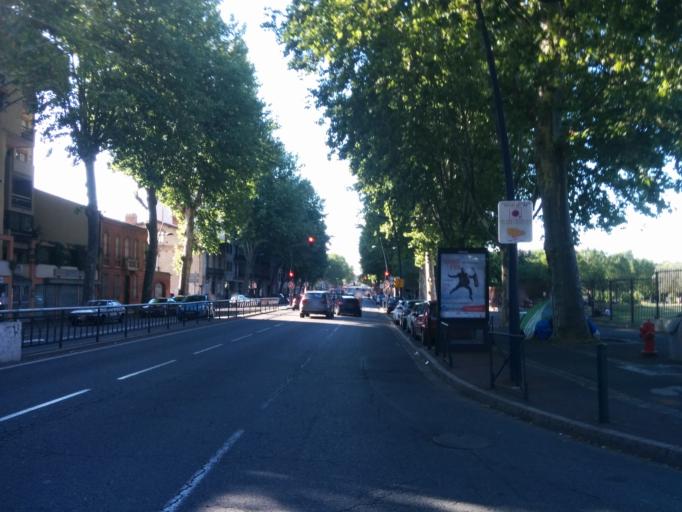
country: FR
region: Midi-Pyrenees
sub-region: Departement de la Haute-Garonne
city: Toulouse
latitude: 43.5987
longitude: 1.4300
